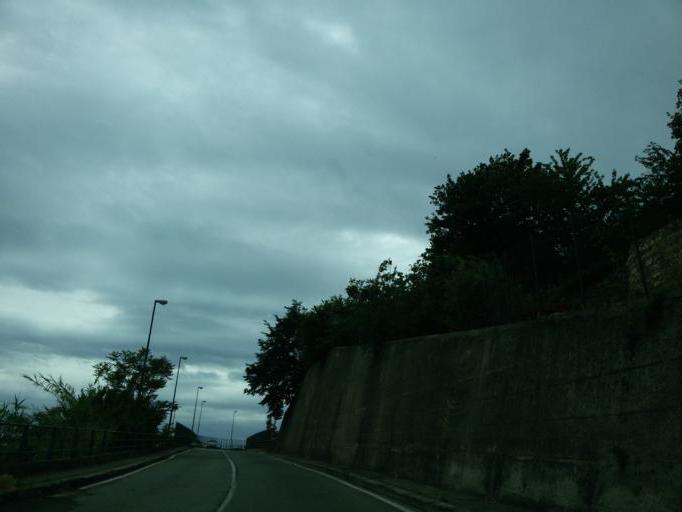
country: IT
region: Liguria
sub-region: Provincia di Genova
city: Piccarello
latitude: 44.4380
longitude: 8.9730
